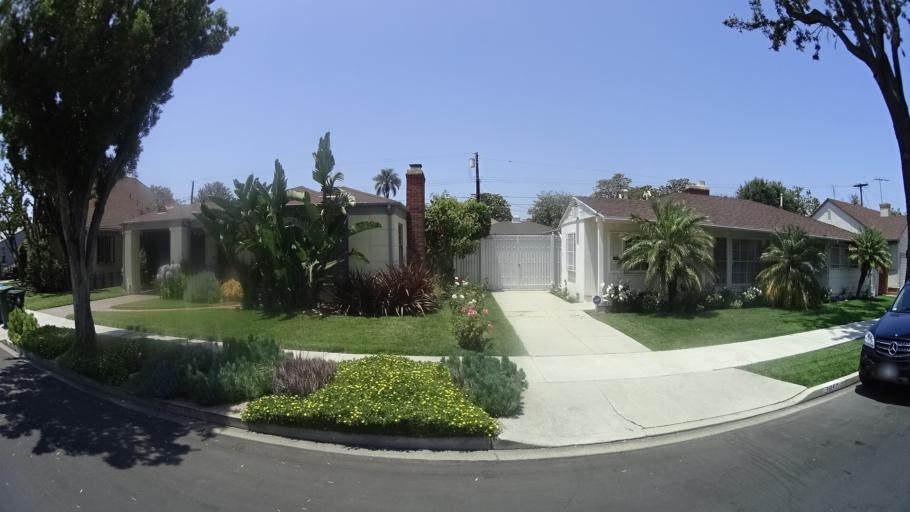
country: US
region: California
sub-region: Los Angeles County
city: View Park-Windsor Hills
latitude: 34.0128
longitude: -118.3281
